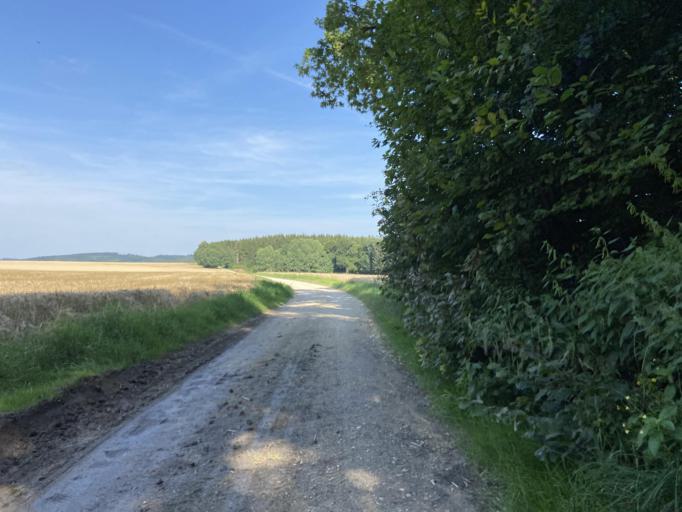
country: DE
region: Baden-Wuerttemberg
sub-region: Tuebingen Region
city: Bingen
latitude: 48.0969
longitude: 9.2624
